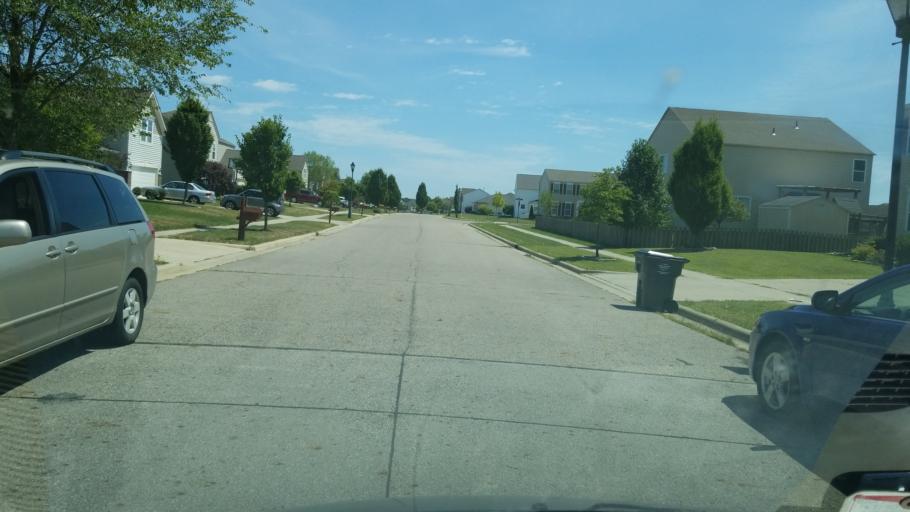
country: US
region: Ohio
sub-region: Franklin County
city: Grove City
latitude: 39.8655
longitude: -83.0935
